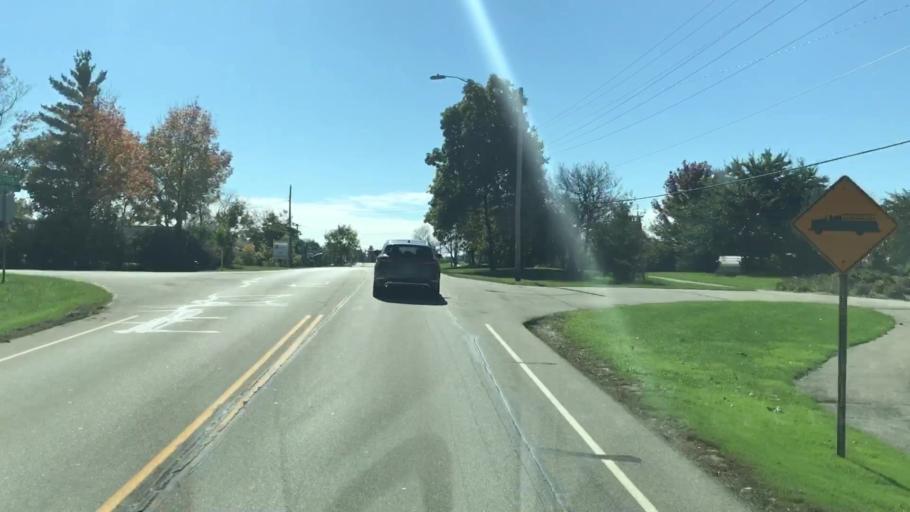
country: US
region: Wisconsin
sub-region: Waukesha County
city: Brookfield
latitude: 43.0939
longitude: -88.1256
